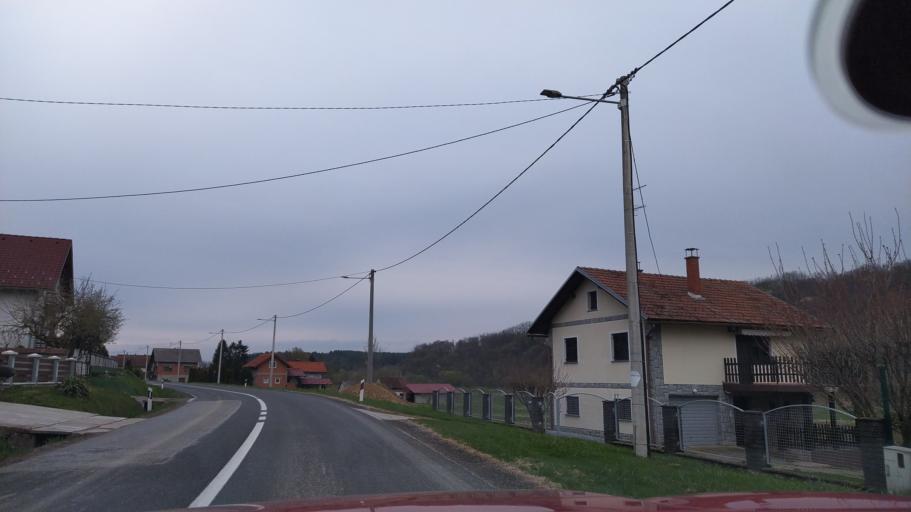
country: HR
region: Varazdinska
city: Jalzabet
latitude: 46.2240
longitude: 16.5414
